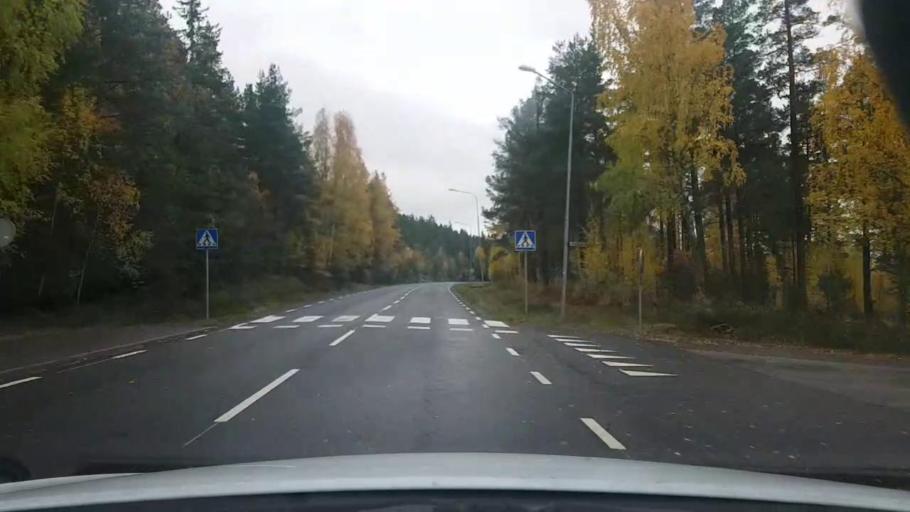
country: SE
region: OErebro
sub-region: Laxa Kommun
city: Laxa
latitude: 58.7771
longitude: 14.5362
